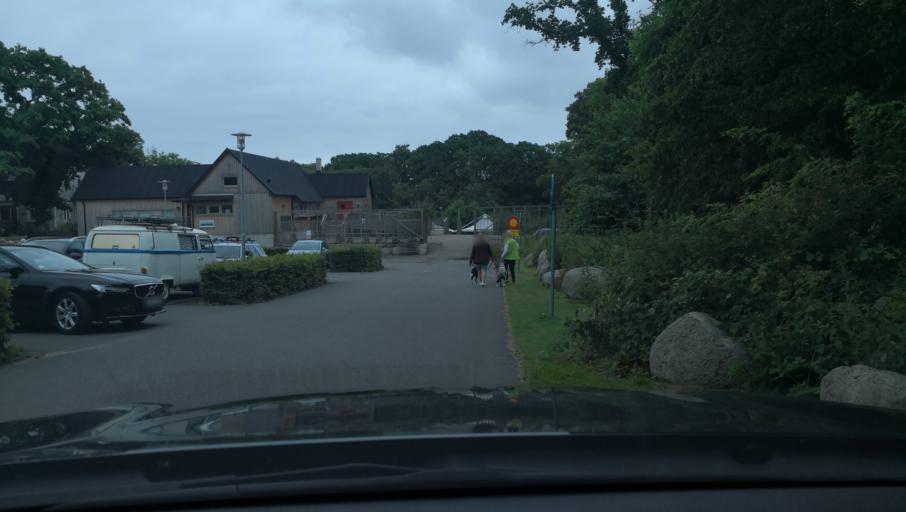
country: SE
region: Skane
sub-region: Simrishamns Kommun
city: Kivik
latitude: 55.6718
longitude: 14.2679
